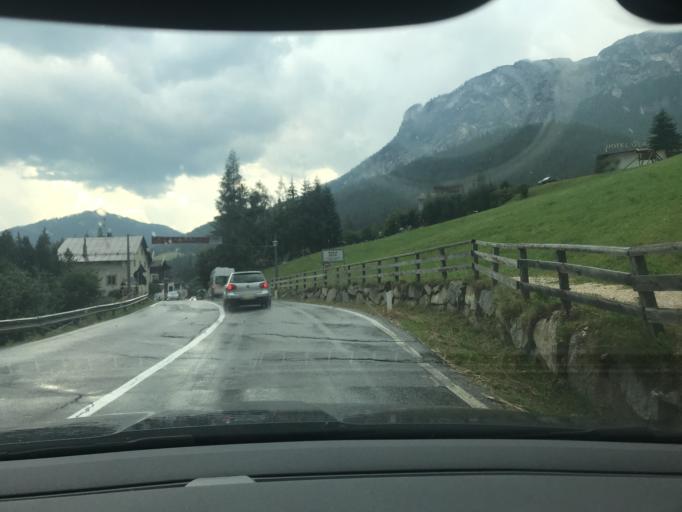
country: IT
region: Trentino-Alto Adige
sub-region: Bolzano
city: Badia
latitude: 46.6126
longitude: 11.8937
